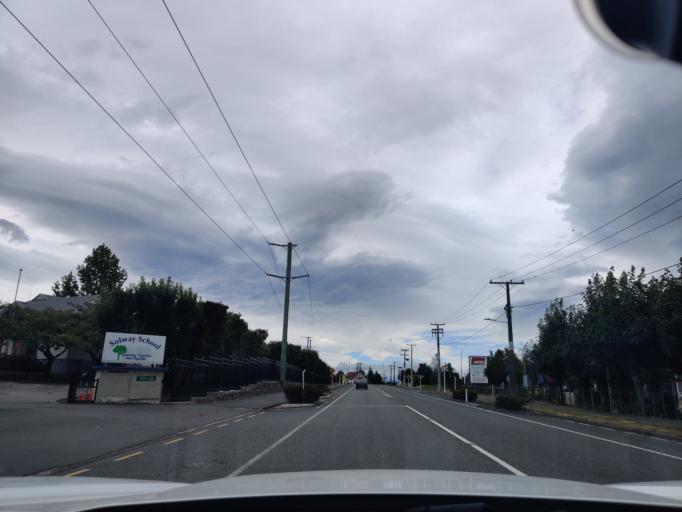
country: NZ
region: Wellington
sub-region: Masterton District
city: Masterton
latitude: -40.9605
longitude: 175.6133
